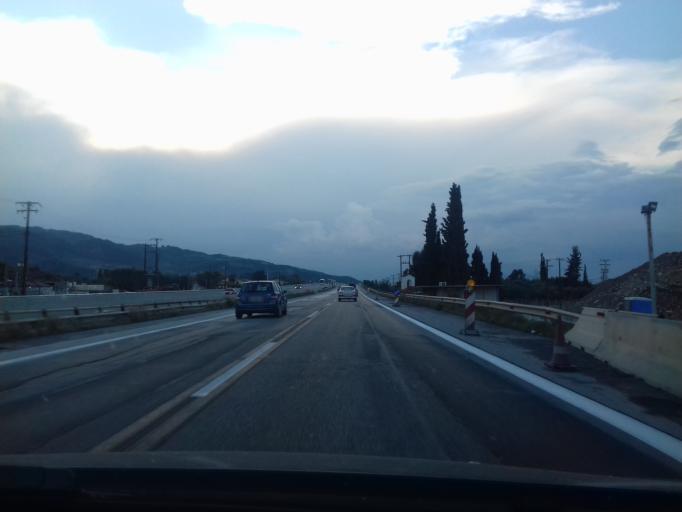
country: GR
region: West Greece
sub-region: Nomos Achaias
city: Kamarai
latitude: 38.2920
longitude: 22.0126
